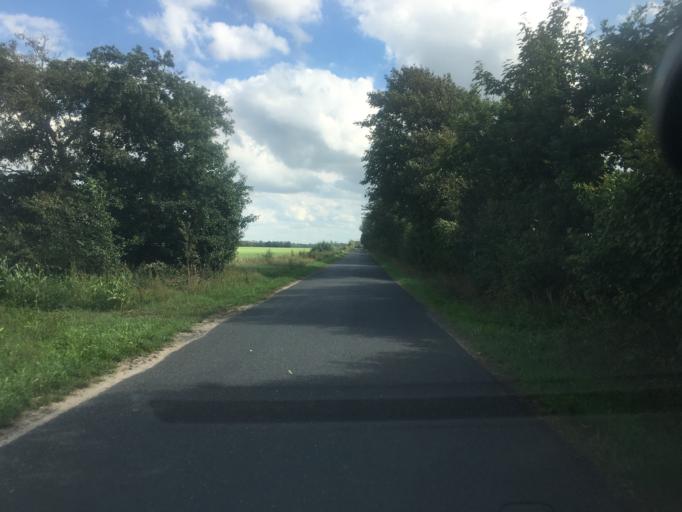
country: DK
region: South Denmark
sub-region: Tonder Kommune
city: Logumkloster
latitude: 55.0091
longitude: 9.0059
